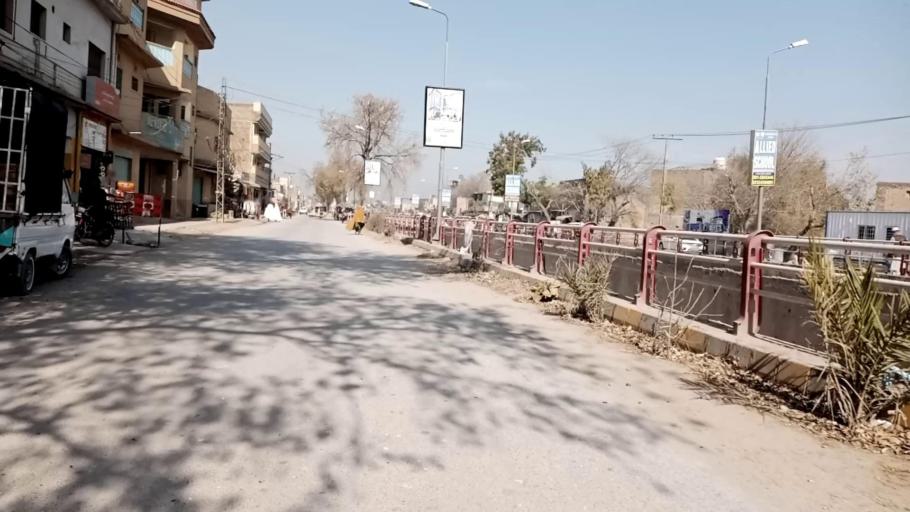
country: PK
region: Khyber Pakhtunkhwa
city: Peshawar
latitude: 33.9824
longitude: 71.4999
